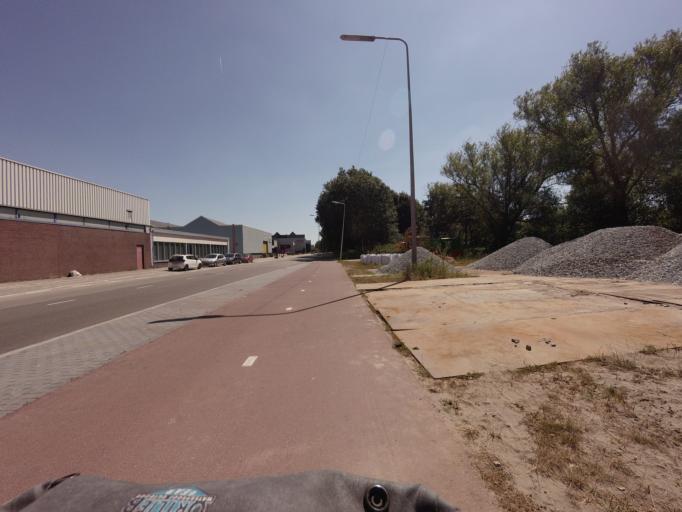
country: NL
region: Utrecht
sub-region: Stichtse Vecht
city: Maarssen
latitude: 52.0994
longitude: 5.0701
